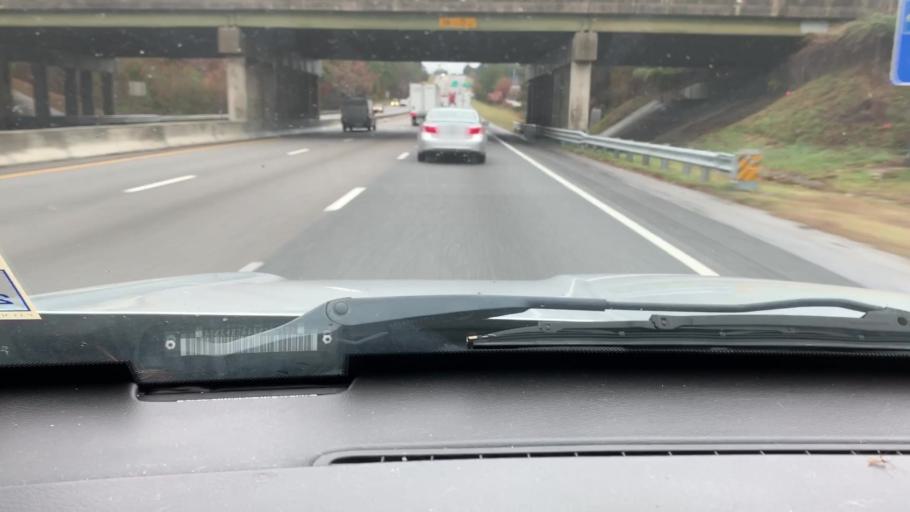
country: US
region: South Carolina
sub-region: Richland County
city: Dentsville
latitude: 34.0738
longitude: -80.9592
